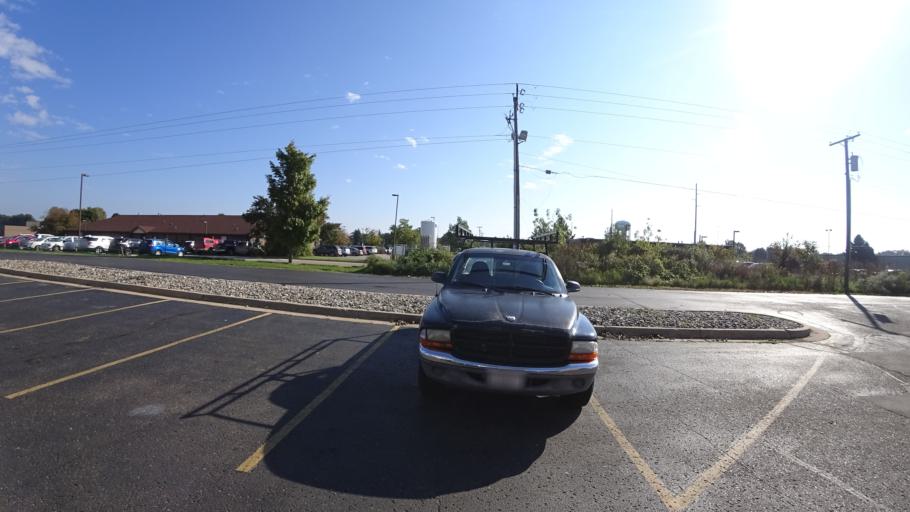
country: US
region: Michigan
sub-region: Saint Joseph County
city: Three Rivers
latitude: 41.9344
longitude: -85.6494
